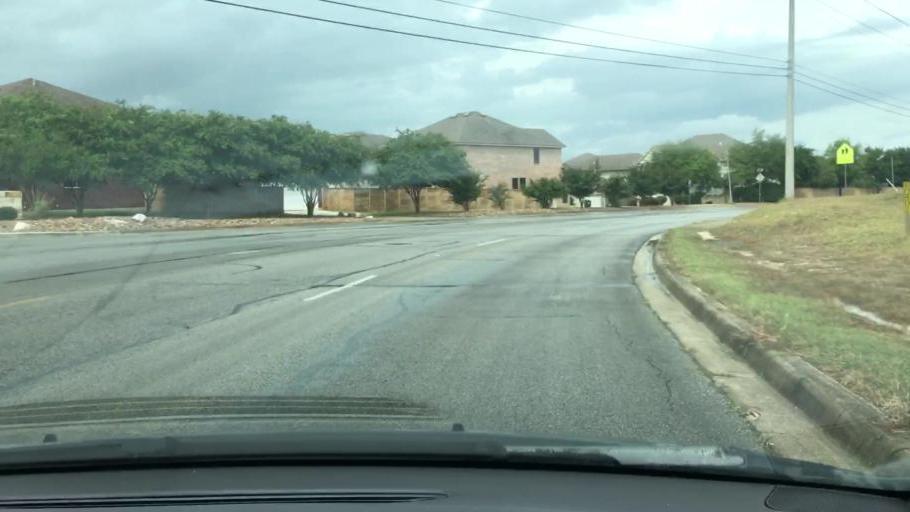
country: US
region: Texas
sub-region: Guadalupe County
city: Northcliff
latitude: 29.5956
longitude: -98.2539
